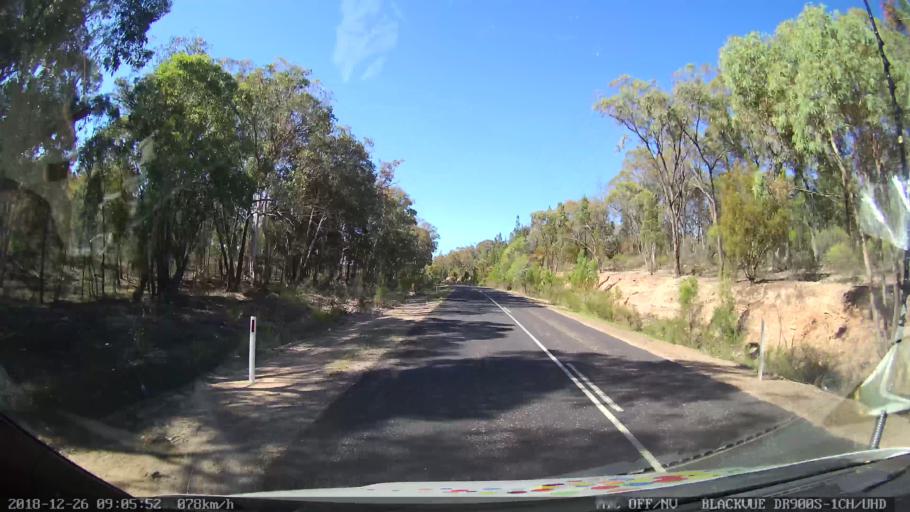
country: AU
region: New South Wales
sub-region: Mid-Western Regional
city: Kandos
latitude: -32.6874
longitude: 150.0052
